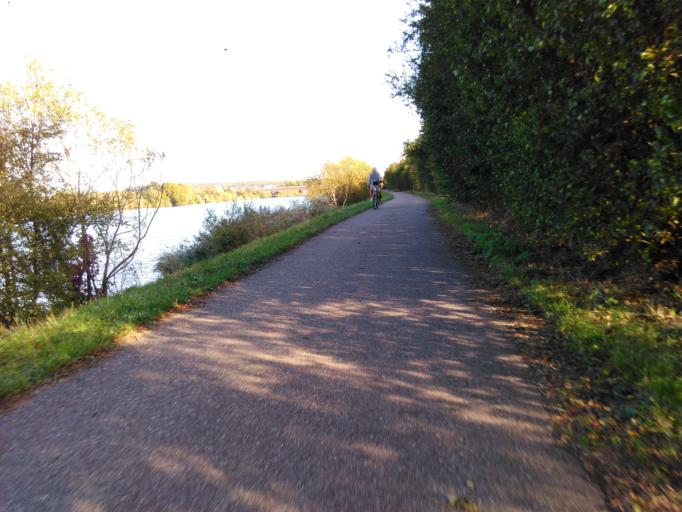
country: FR
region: Lorraine
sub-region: Departement de la Moselle
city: Bertrange
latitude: 49.2970
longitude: 6.1706
